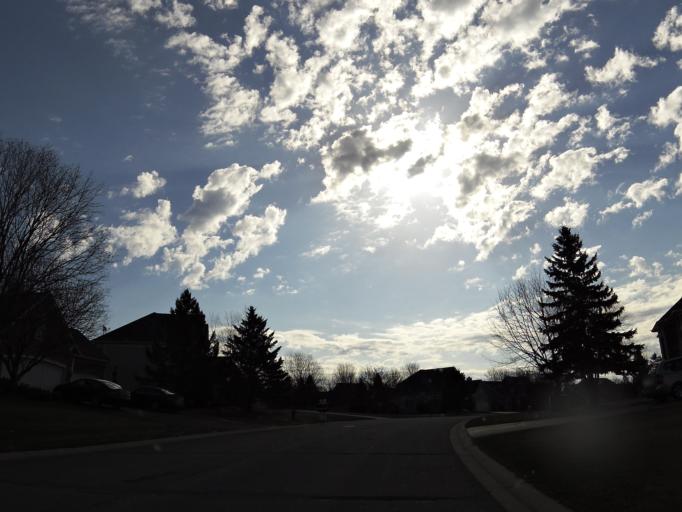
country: US
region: Minnesota
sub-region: Washington County
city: Woodbury
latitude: 44.8993
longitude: -92.8970
